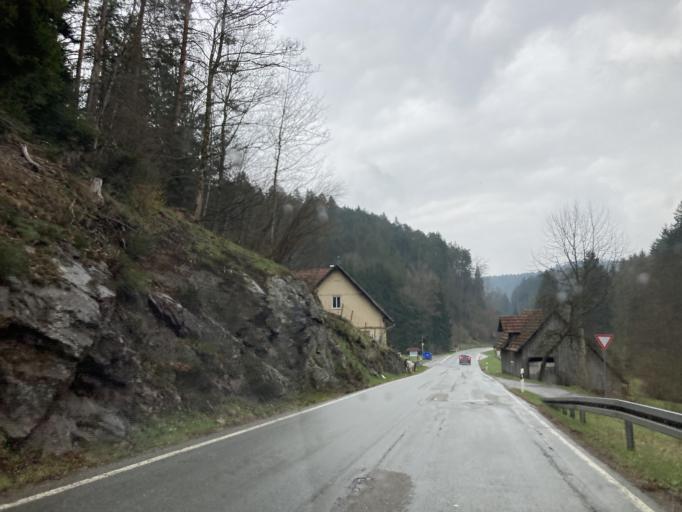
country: DE
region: Baden-Wuerttemberg
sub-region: Freiburg Region
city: Lauterbach/Schwarzwald
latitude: 48.2286
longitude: 8.3175
